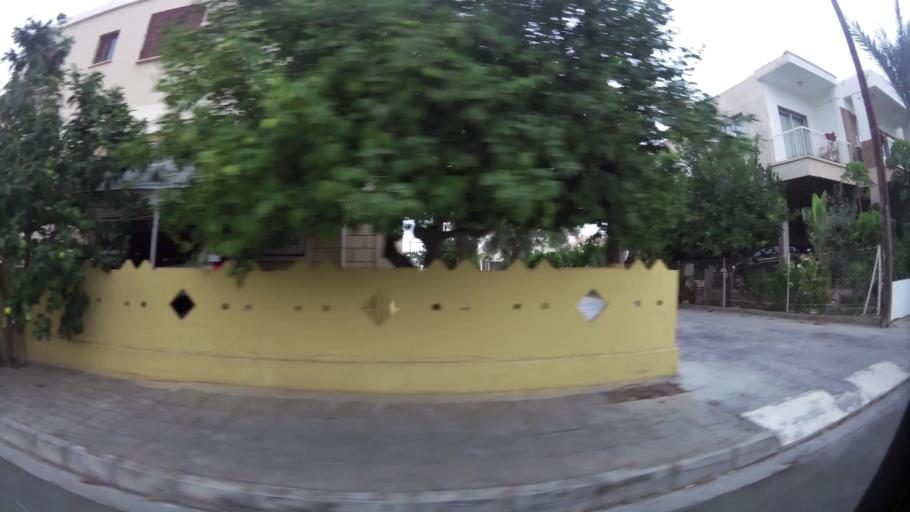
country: CY
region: Lefkosia
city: Geri
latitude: 35.1002
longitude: 33.3818
